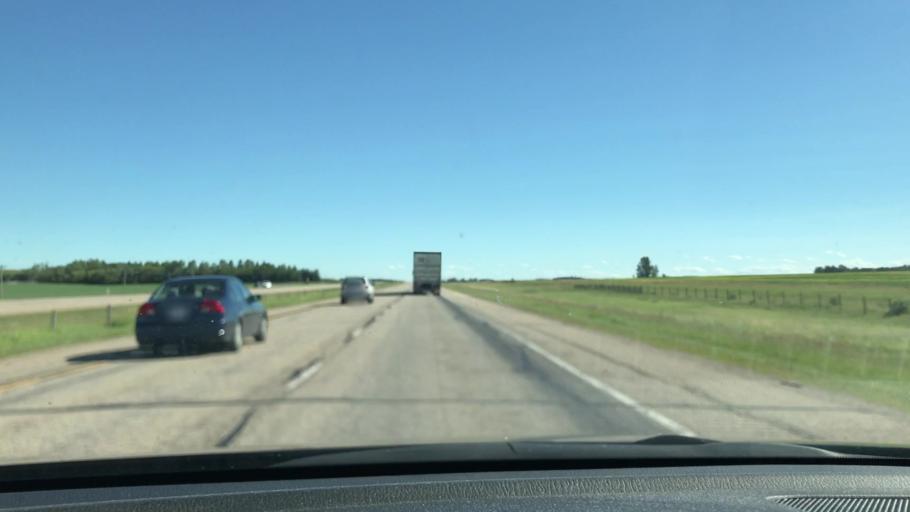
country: CA
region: Alberta
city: Olds
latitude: 51.8641
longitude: -114.0257
